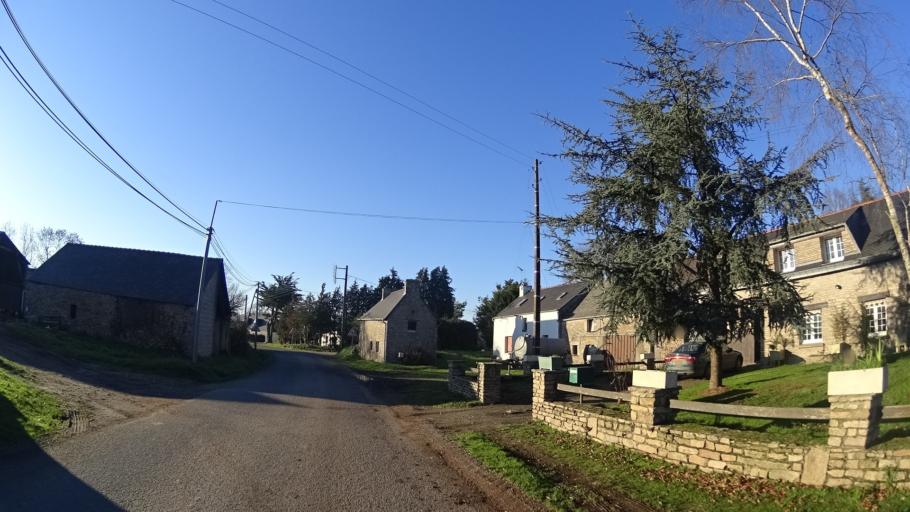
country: FR
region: Brittany
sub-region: Departement du Morbihan
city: Allaire
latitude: 47.6521
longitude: -2.1526
